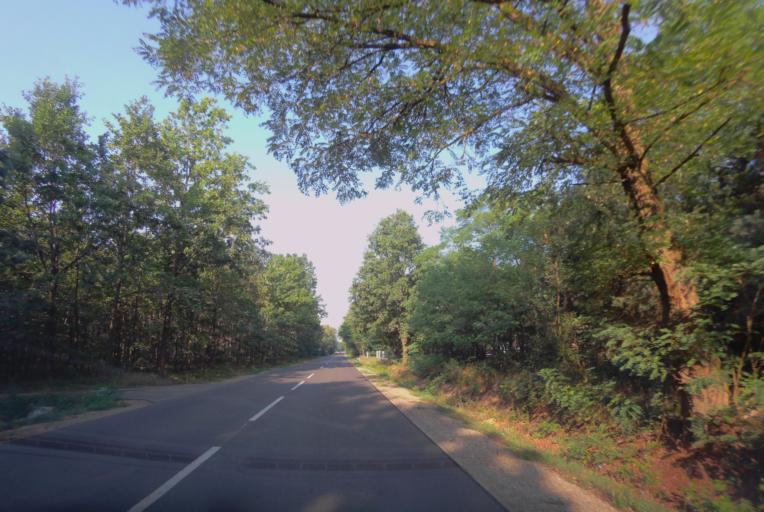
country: PL
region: Subcarpathian Voivodeship
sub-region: Powiat nizanski
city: Jarocin
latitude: 50.5100
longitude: 22.3229
